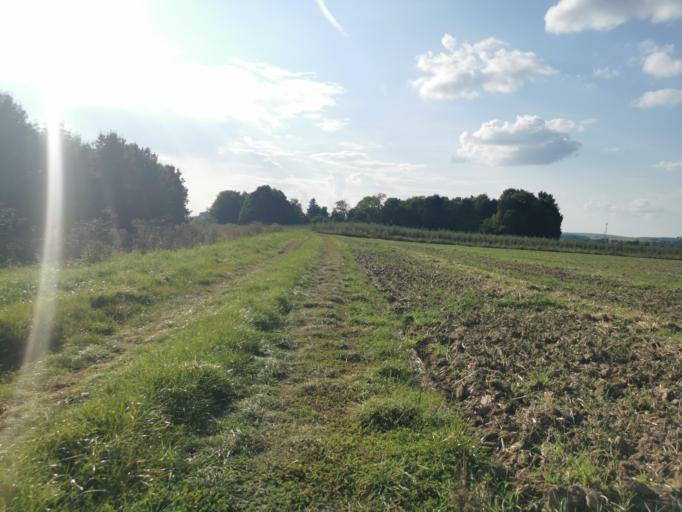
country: SK
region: Trnavsky
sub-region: Okres Senica
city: Senica
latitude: 48.6687
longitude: 17.2809
